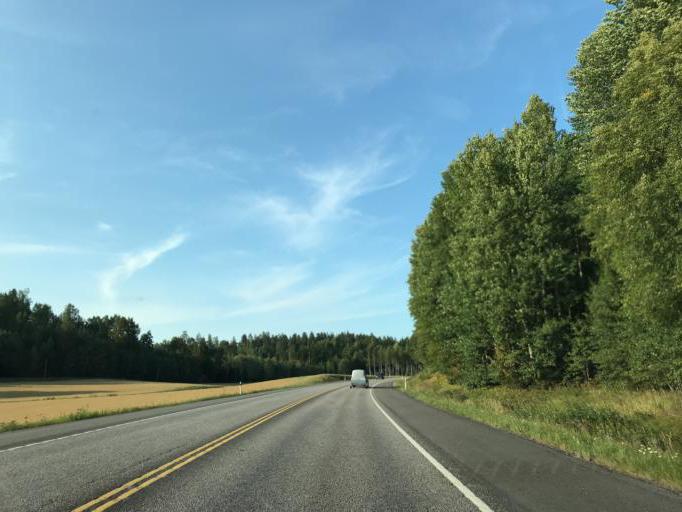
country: FI
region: Uusimaa
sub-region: Helsinki
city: Vihti
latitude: 60.3860
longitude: 24.3178
